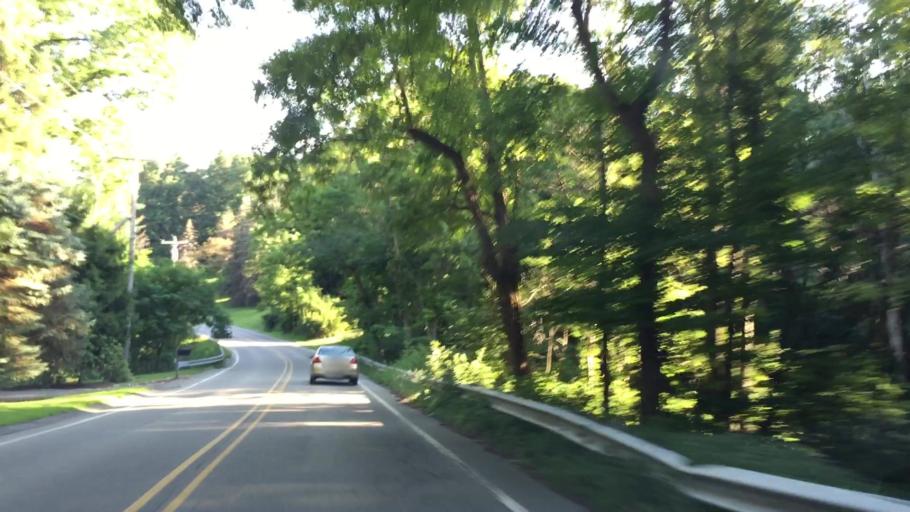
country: US
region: Pennsylvania
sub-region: Allegheny County
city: Franklin Park
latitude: 40.5783
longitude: -80.0722
